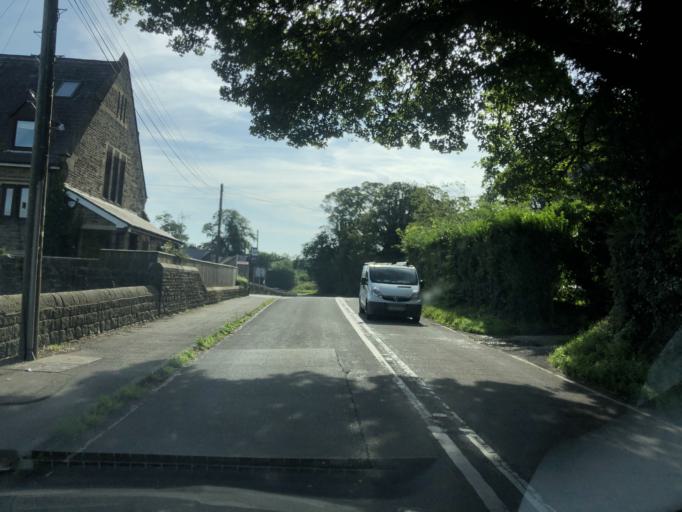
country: GB
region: England
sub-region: City and Borough of Leeds
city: Pool
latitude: 53.8981
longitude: -1.6034
